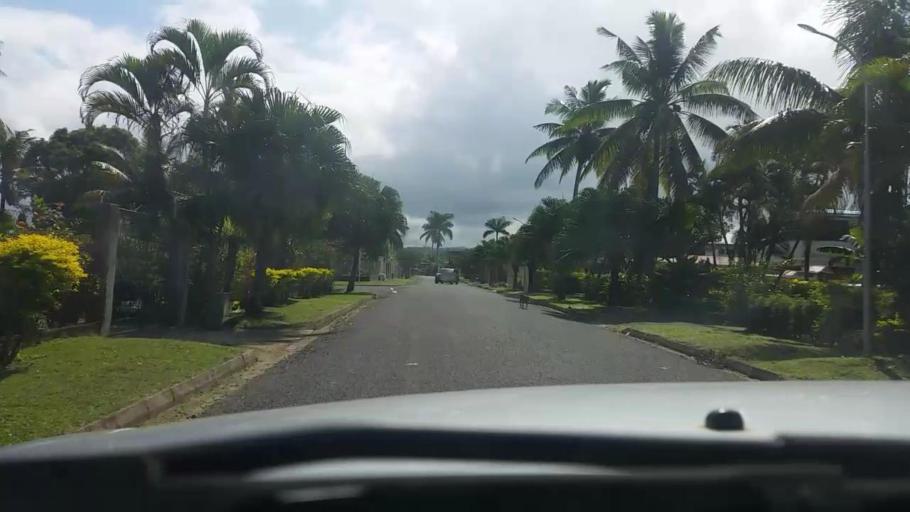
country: FJ
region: Central
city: Suva
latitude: -18.1309
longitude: 178.4657
